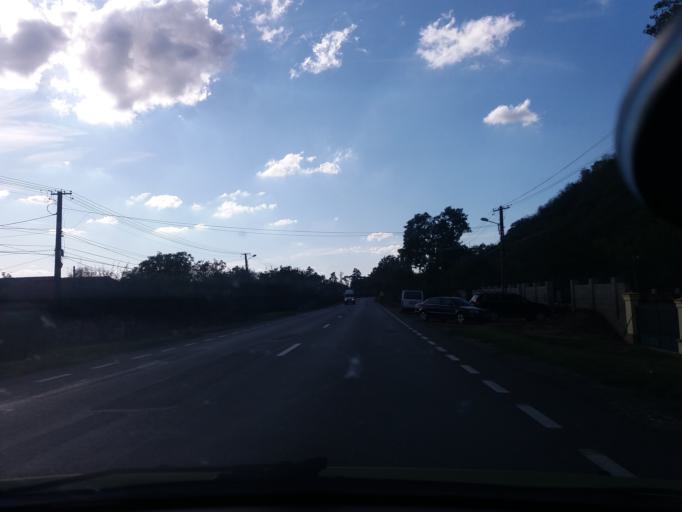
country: RO
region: Arad
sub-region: Comuna Paulis
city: Paulis
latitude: 46.1087
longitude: 21.6057
